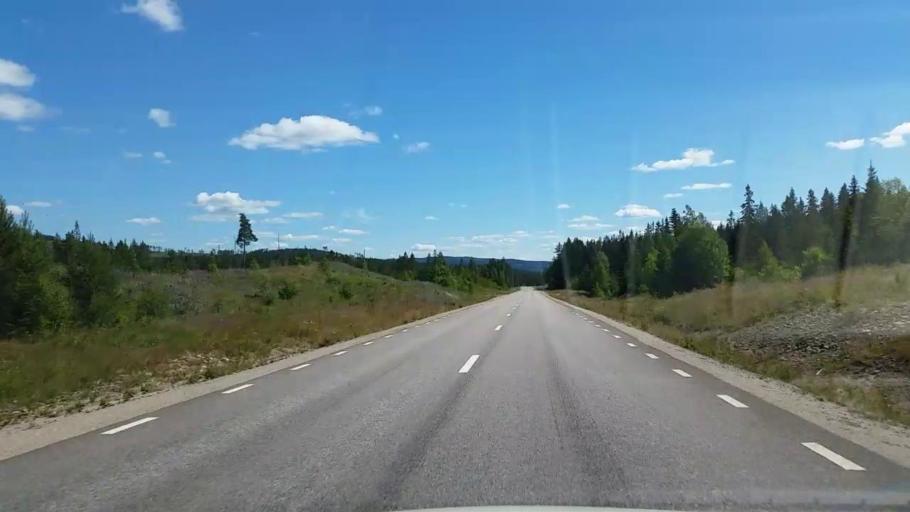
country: SE
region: Gaevleborg
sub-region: Bollnas Kommun
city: Vittsjo
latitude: 61.0672
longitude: 15.7969
